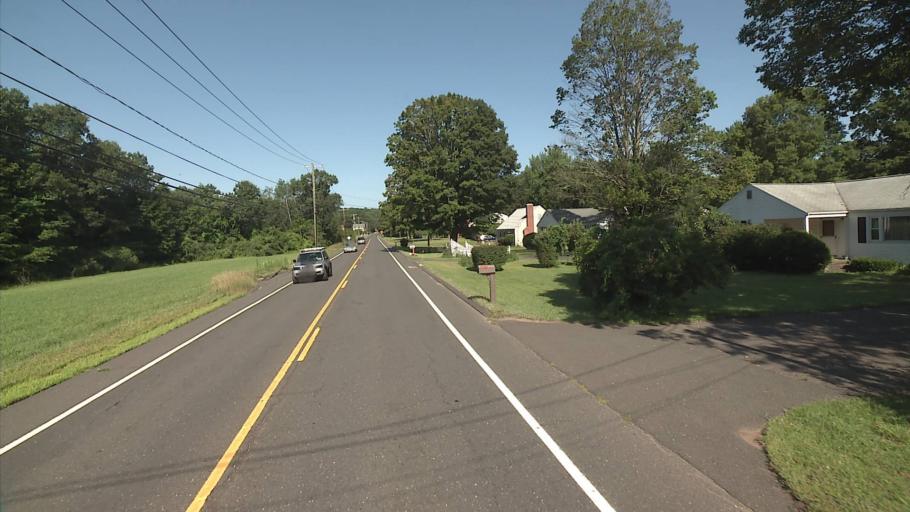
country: US
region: Connecticut
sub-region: Hartford County
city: Salmon Brook
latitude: 41.9523
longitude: -72.8070
